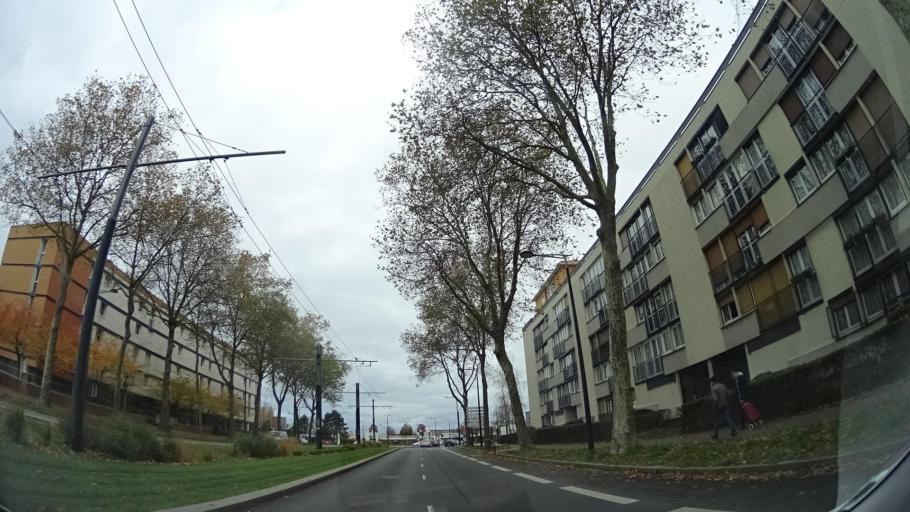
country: FR
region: Haute-Normandie
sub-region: Departement de la Seine-Maritime
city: Le Havre
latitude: 49.5197
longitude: 0.1154
